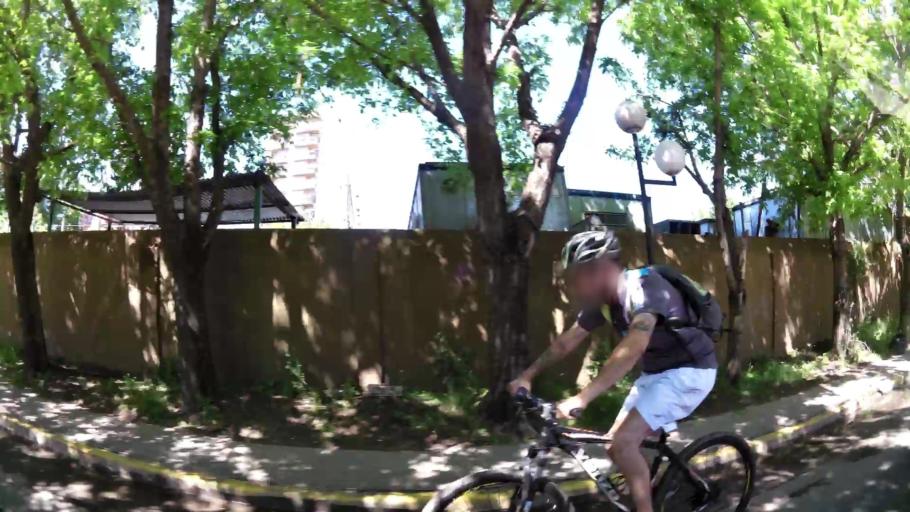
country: AR
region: Buenos Aires
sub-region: Partido de Quilmes
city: Quilmes
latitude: -34.7089
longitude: -58.2809
